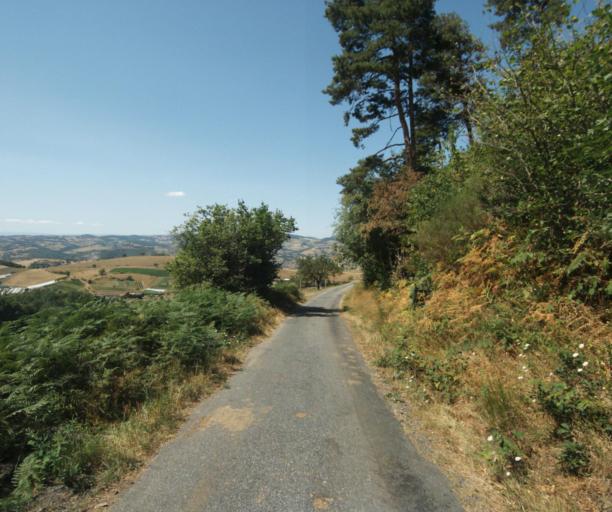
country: FR
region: Rhone-Alpes
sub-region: Departement du Rhone
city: Courzieu
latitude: 45.7191
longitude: 4.5483
